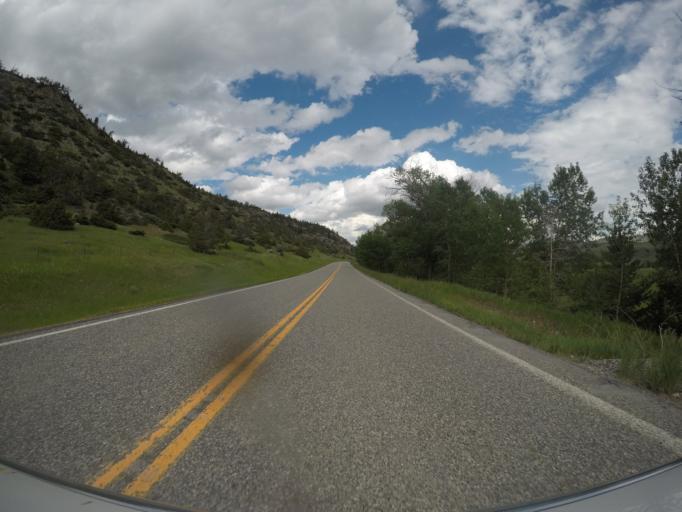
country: US
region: Montana
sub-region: Sweet Grass County
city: Big Timber
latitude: 45.6687
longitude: -110.1057
